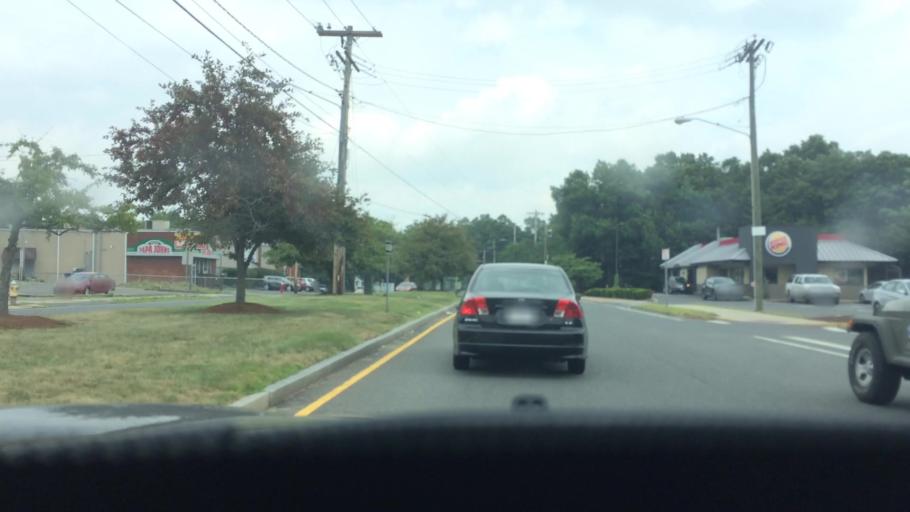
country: US
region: Massachusetts
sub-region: Hampden County
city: Chicopee
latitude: 42.1395
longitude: -72.5823
